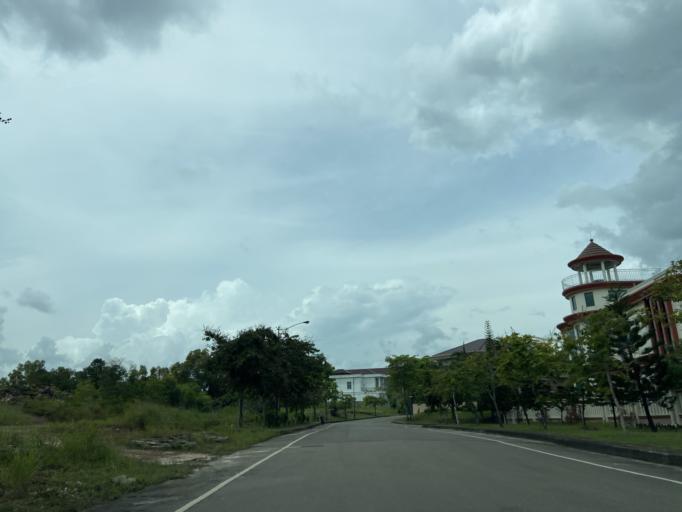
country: SG
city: Singapore
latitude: 1.1292
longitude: 103.9999
